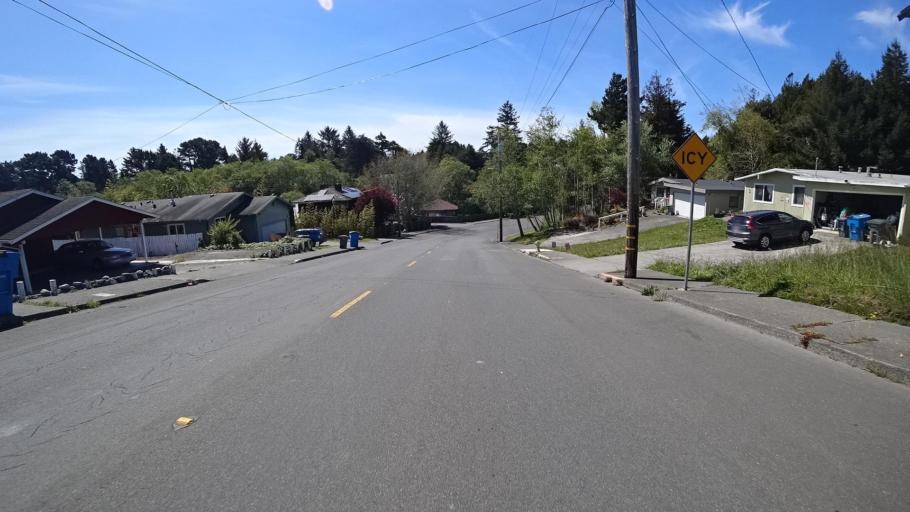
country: US
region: California
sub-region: Humboldt County
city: Myrtletown
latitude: 40.7919
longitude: -124.1482
